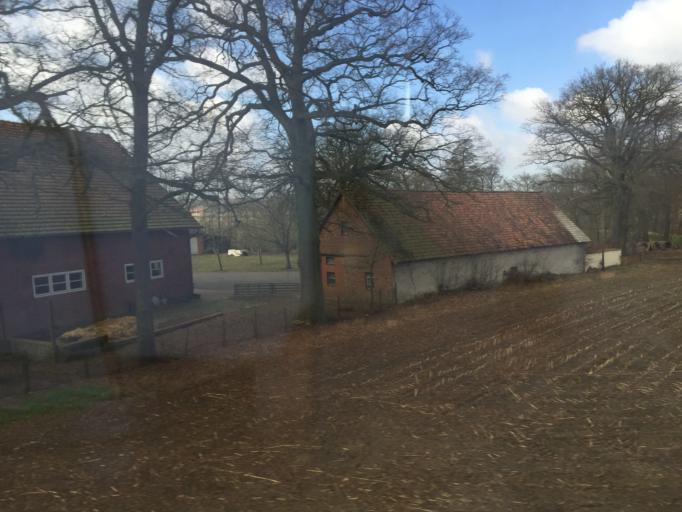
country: DE
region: Lower Saxony
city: Hasbergen
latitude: 52.2247
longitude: 7.9201
